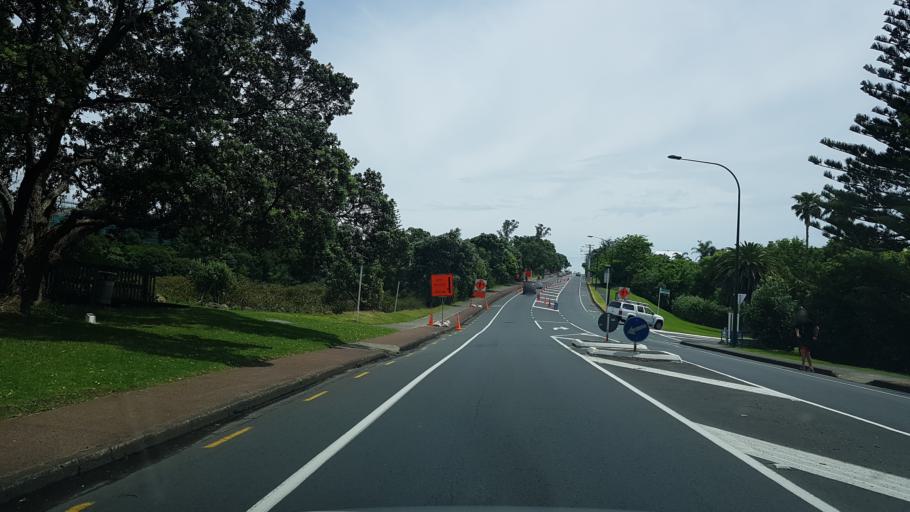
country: NZ
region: Auckland
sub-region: Auckland
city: North Shore
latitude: -36.8183
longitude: 174.7950
